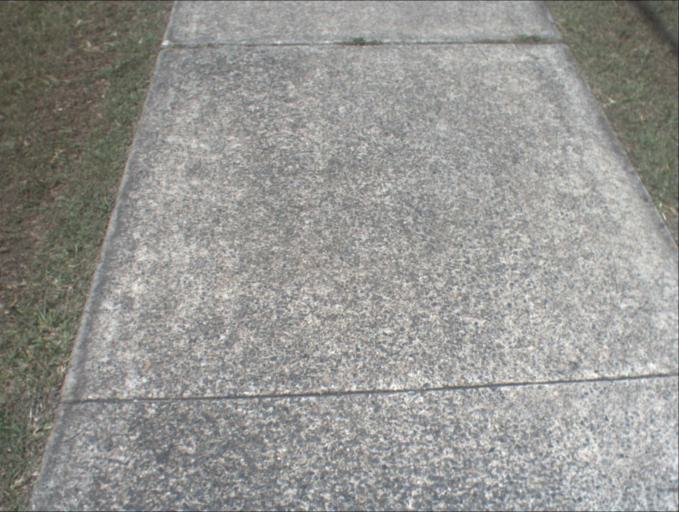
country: AU
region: Queensland
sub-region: Logan
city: Windaroo
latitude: -27.7545
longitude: 153.1865
